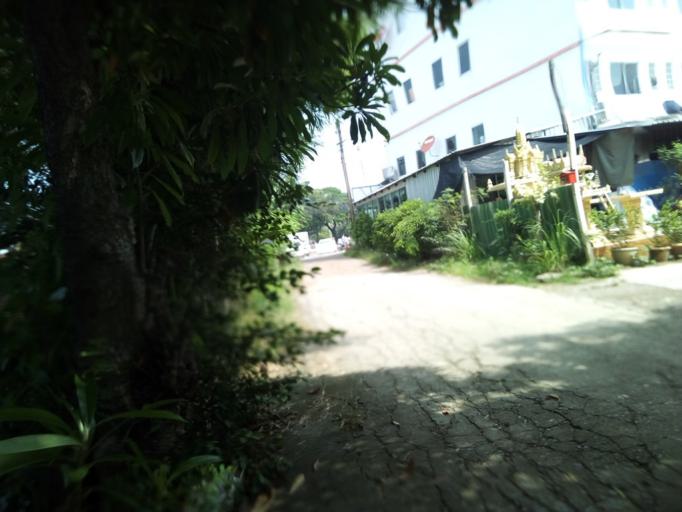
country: TH
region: Pathum Thani
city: Nong Suea
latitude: 14.0622
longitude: 100.8548
